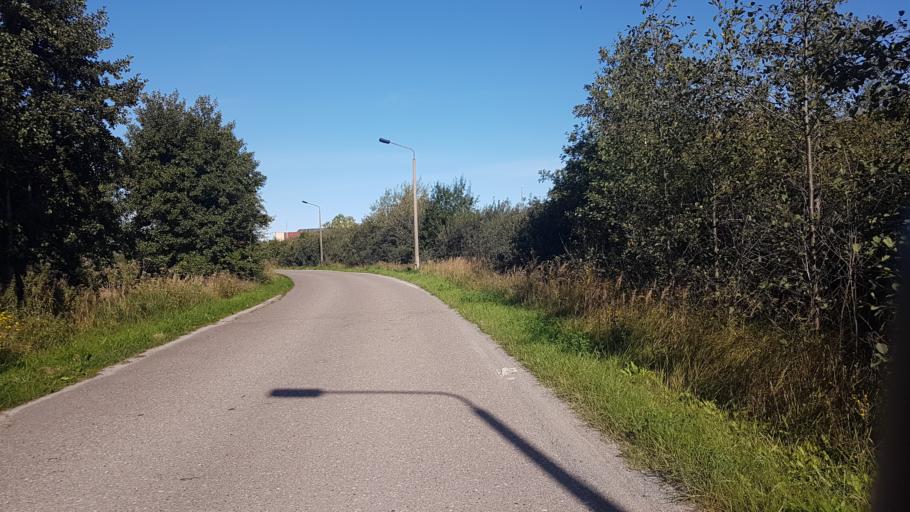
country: DE
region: Mecklenburg-Vorpommern
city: Sagard
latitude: 54.4959
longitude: 13.5524
